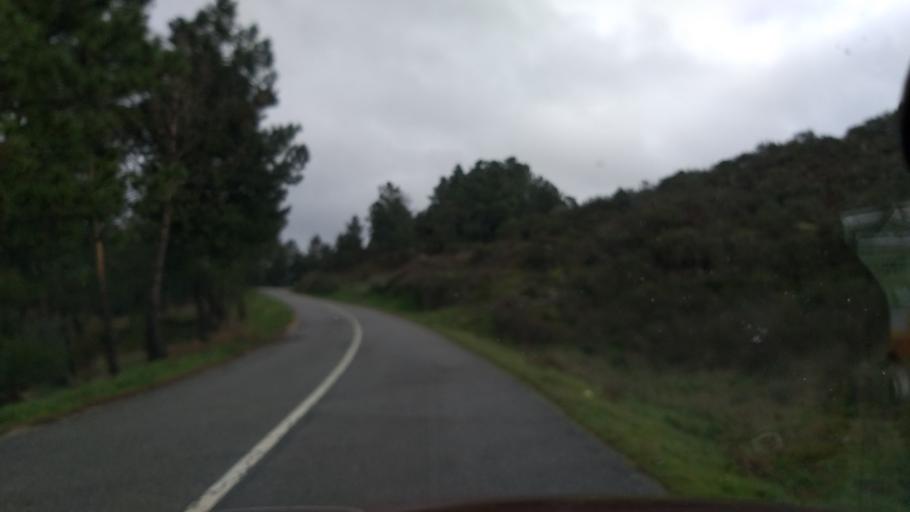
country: PT
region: Guarda
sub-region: Celorico da Beira
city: Celorico da Beira
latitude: 40.7065
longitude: -7.4281
